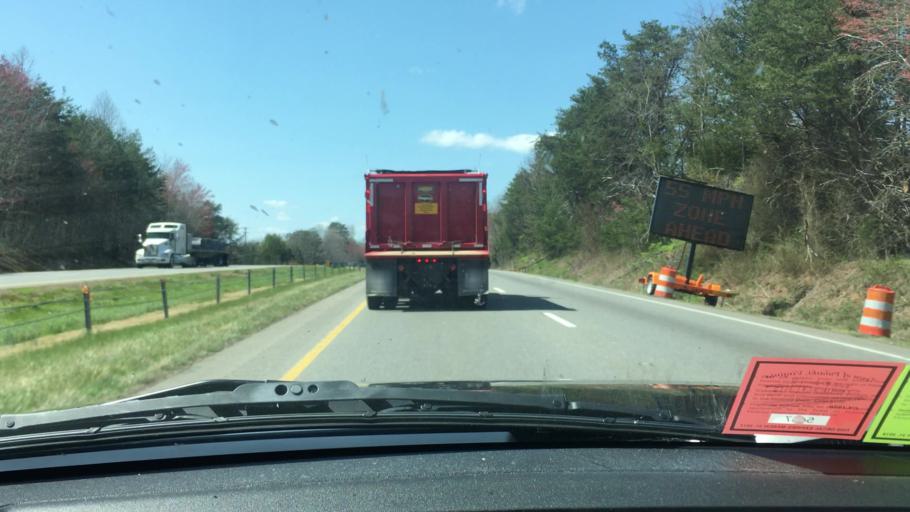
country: US
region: North Carolina
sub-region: Surry County
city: Pilot Mountain
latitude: 36.4280
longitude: -80.5229
